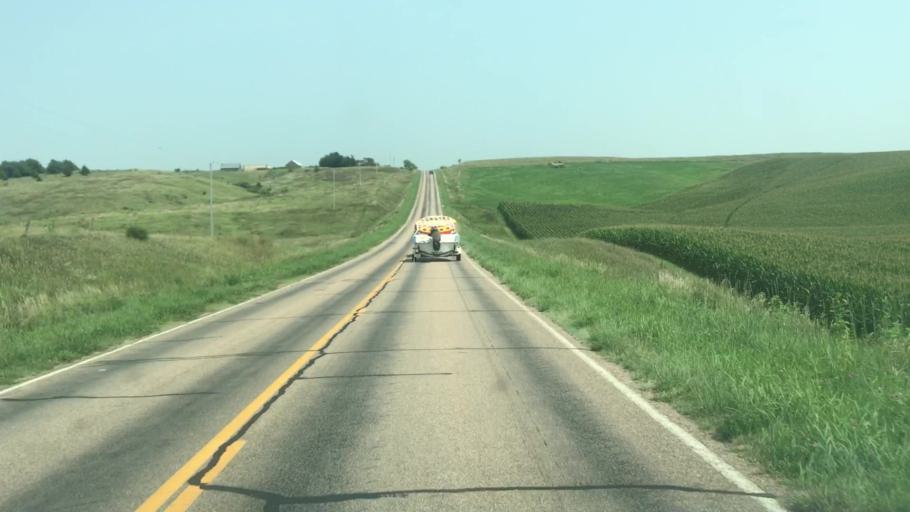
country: US
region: Nebraska
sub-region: Sherman County
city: Loup City
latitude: 41.2792
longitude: -98.9144
